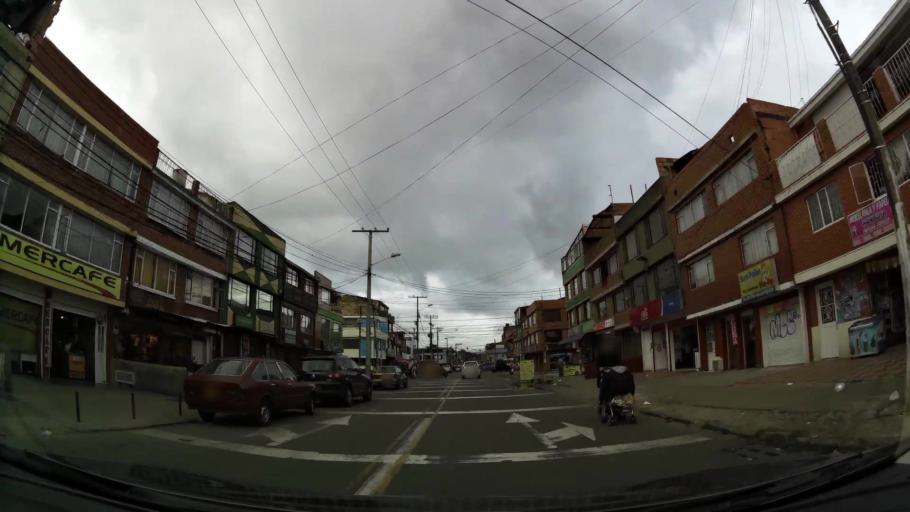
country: CO
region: Bogota D.C.
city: Barrio San Luis
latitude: 4.6917
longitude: -74.1022
